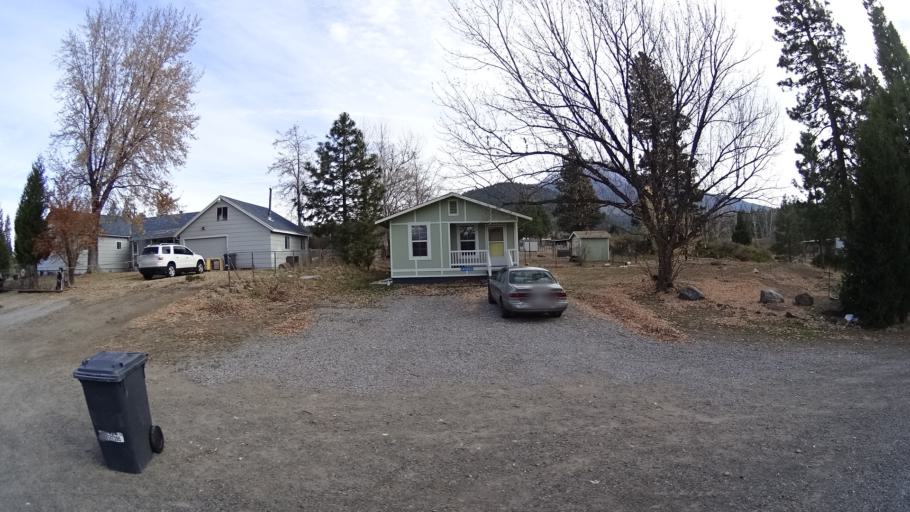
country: US
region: California
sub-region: Siskiyou County
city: Weed
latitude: 41.4492
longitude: -122.3587
